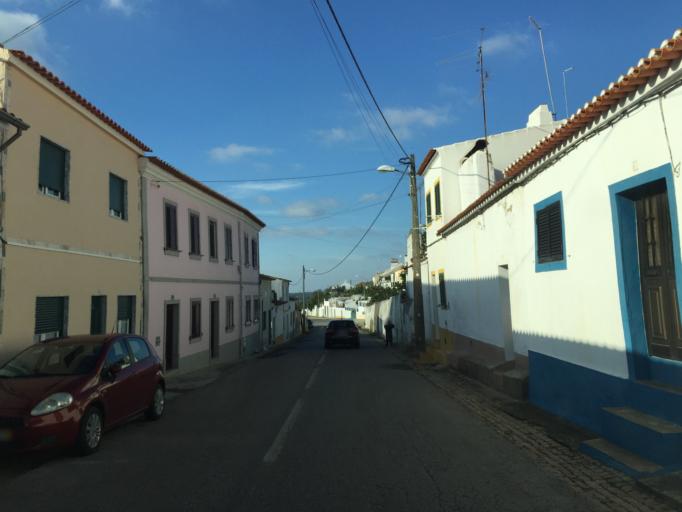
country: PT
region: Portalegre
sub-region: Fronteira
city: Fronteira
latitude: 39.0588
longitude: -7.6498
